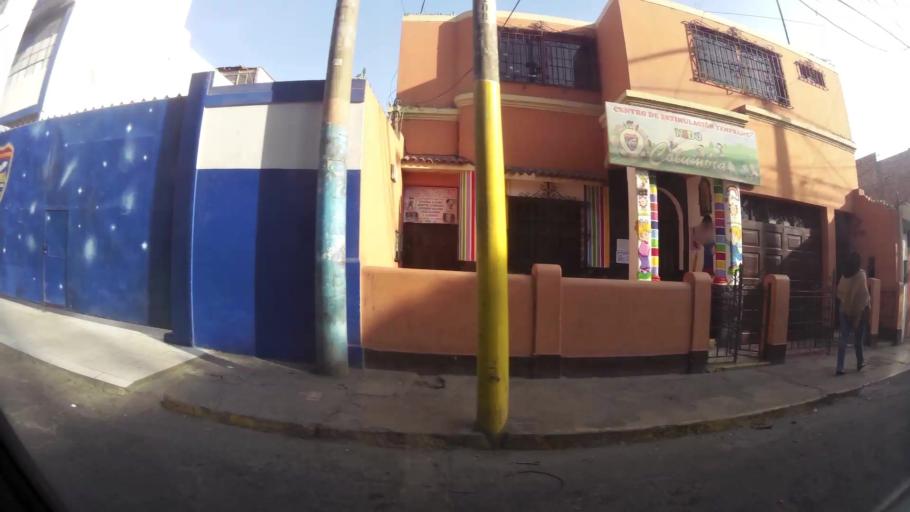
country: PE
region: Lima
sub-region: Huaura
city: Huacho
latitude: -11.1079
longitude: -77.6033
